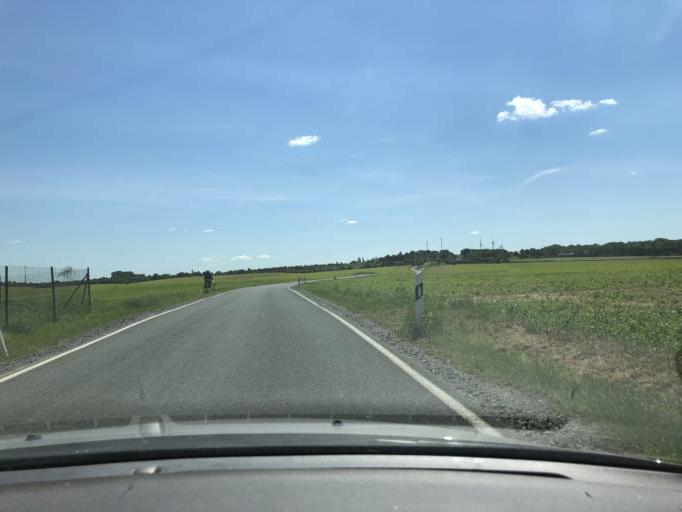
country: DE
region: Saxony
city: Nerchau
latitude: 51.2583
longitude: 12.8000
